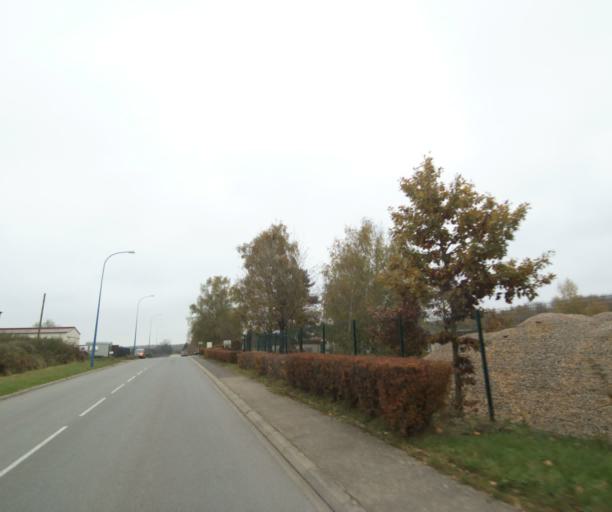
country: FR
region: Lorraine
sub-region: Departement de Meurthe-et-Moselle
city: Moutiers
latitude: 49.2540
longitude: 5.9662
